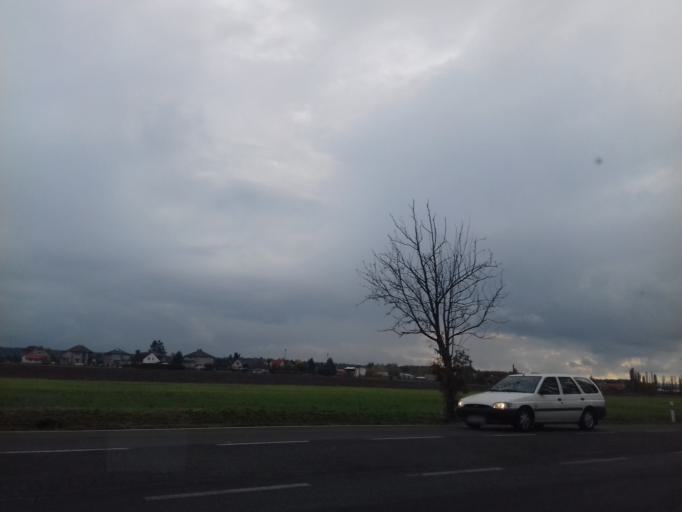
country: CZ
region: Pardubicky
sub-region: Okres Chrudim
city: Chrast
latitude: 49.9054
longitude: 15.9225
